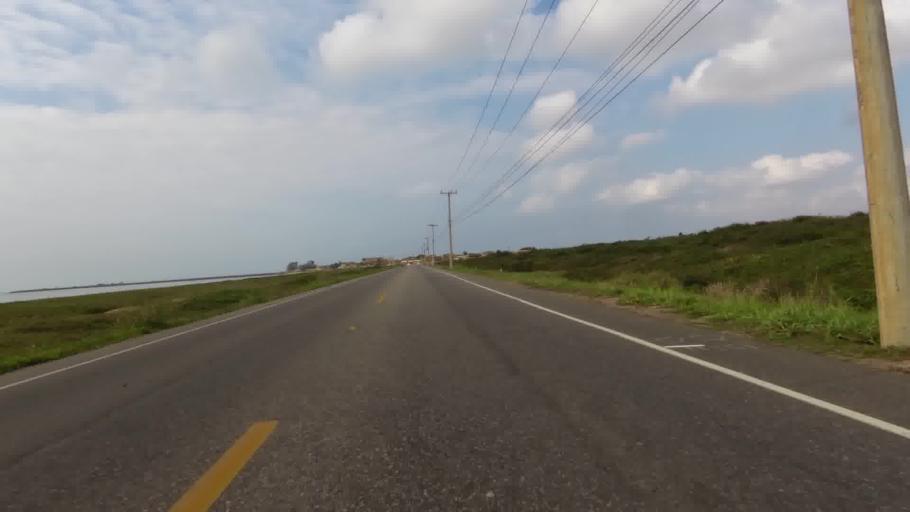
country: BR
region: Espirito Santo
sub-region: Itapemirim
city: Itapemirim
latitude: -20.9944
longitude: -40.8104
